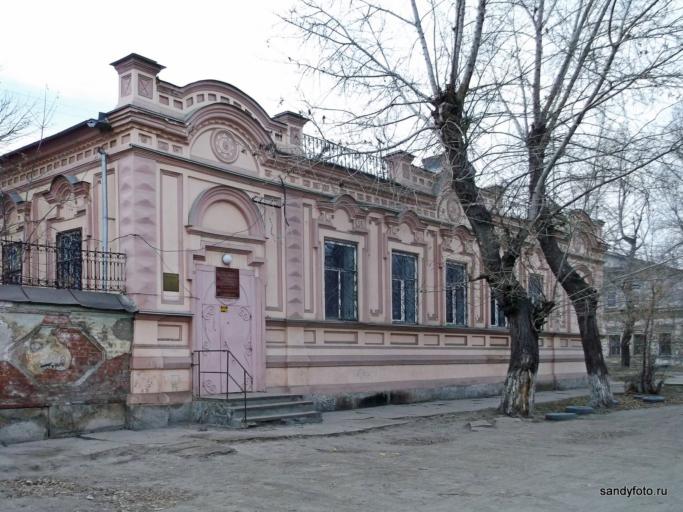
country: RU
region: Chelyabinsk
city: Troitsk
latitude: 54.0795
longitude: 61.5561
